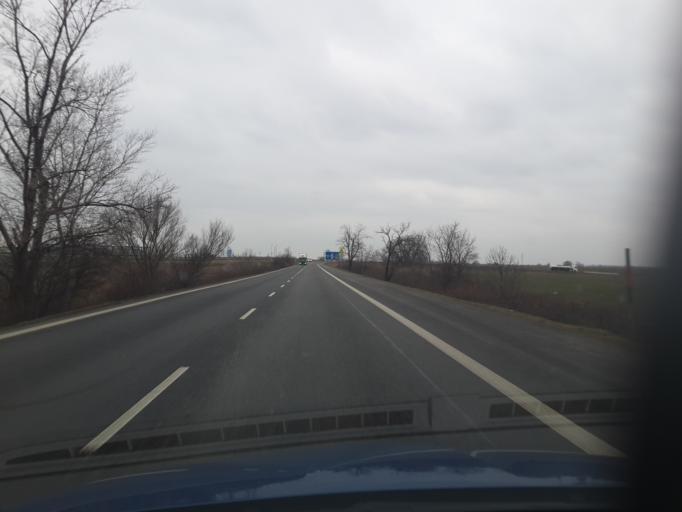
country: SK
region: Bratislavsky
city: Stupava
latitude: 48.2420
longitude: 16.9904
